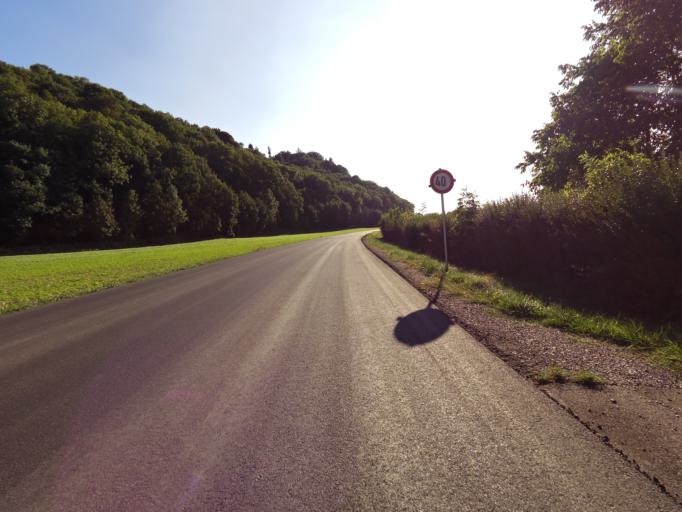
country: DE
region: Bavaria
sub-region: Lower Bavaria
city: Stallwang
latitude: 48.5773
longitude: 12.2394
